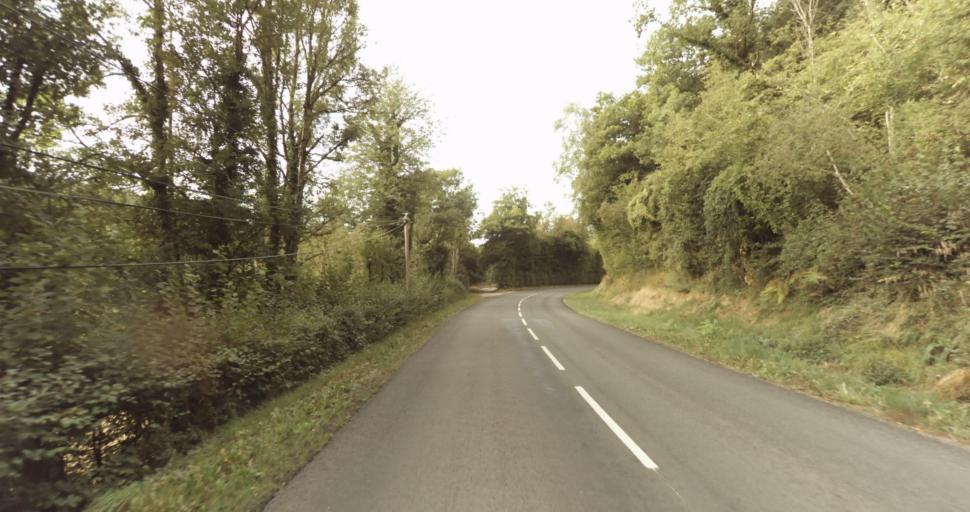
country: FR
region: Lower Normandy
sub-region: Departement de l'Orne
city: Vimoutiers
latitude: 48.9557
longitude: 0.2559
